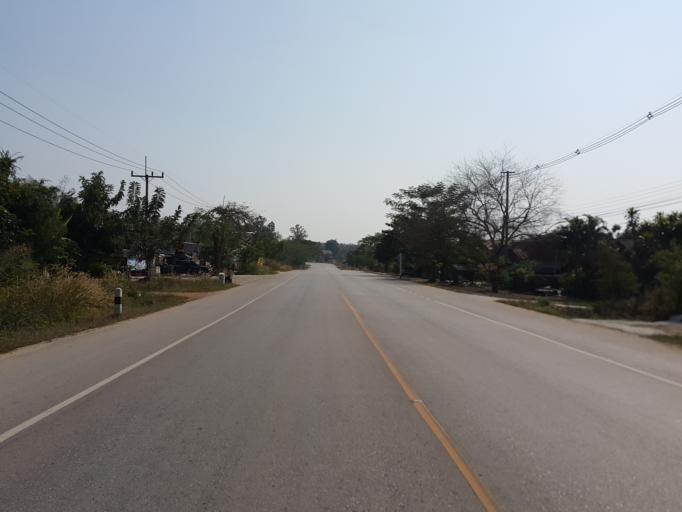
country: TH
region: Lampang
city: Chae Hom
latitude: 18.7429
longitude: 99.5773
